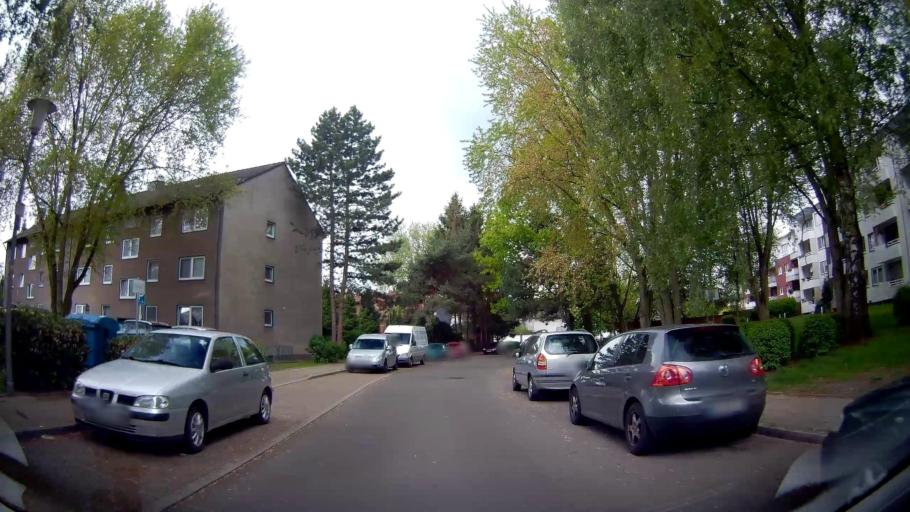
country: DE
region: North Rhine-Westphalia
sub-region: Regierungsbezirk Munster
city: Gladbeck
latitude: 51.5787
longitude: 6.9637
